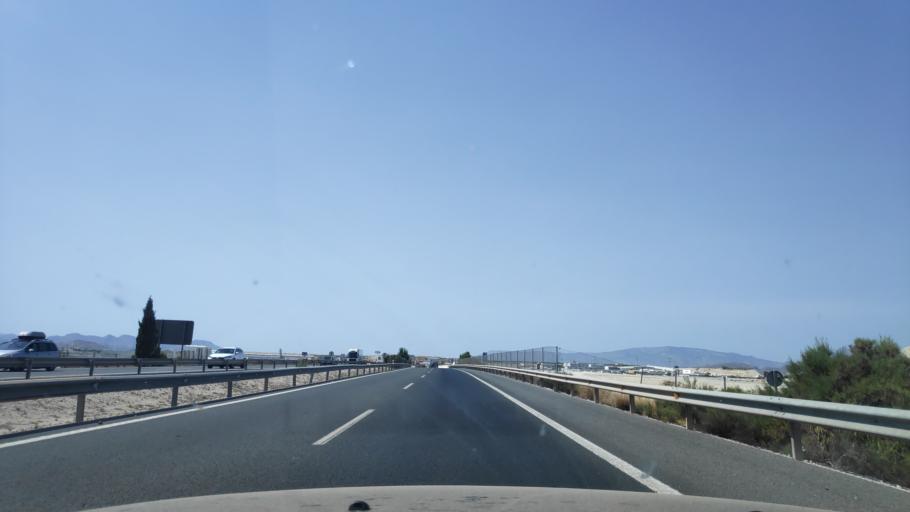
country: ES
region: Murcia
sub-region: Murcia
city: Lorqui
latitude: 38.0936
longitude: -1.2267
